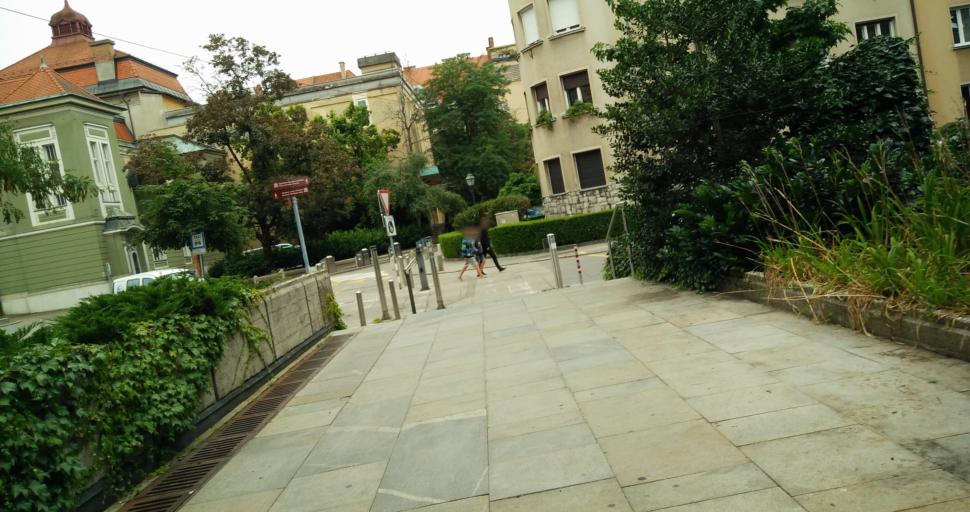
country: SI
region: Ljubljana
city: Ljubljana
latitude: 46.0495
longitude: 14.5012
